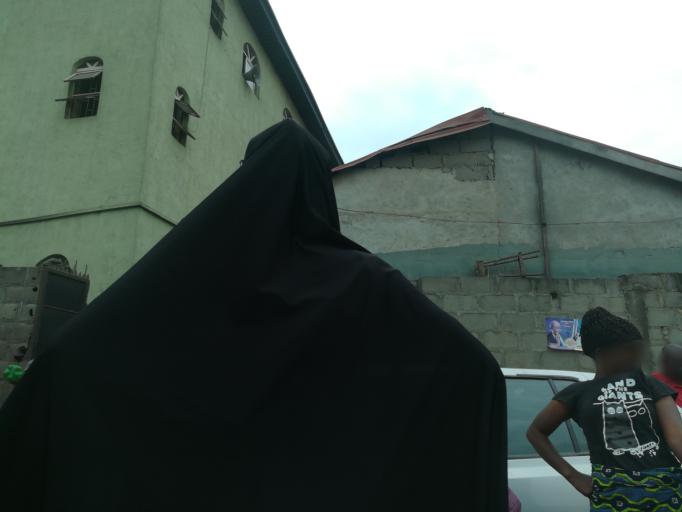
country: NG
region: Lagos
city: Ojota
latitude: 6.6088
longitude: 3.3961
